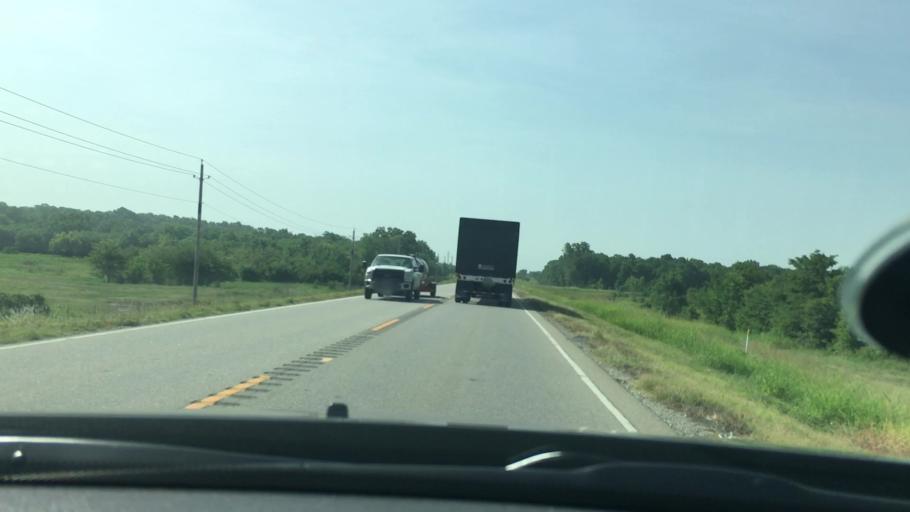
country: US
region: Oklahoma
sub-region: Coal County
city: Coalgate
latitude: 34.4512
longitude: -96.2100
